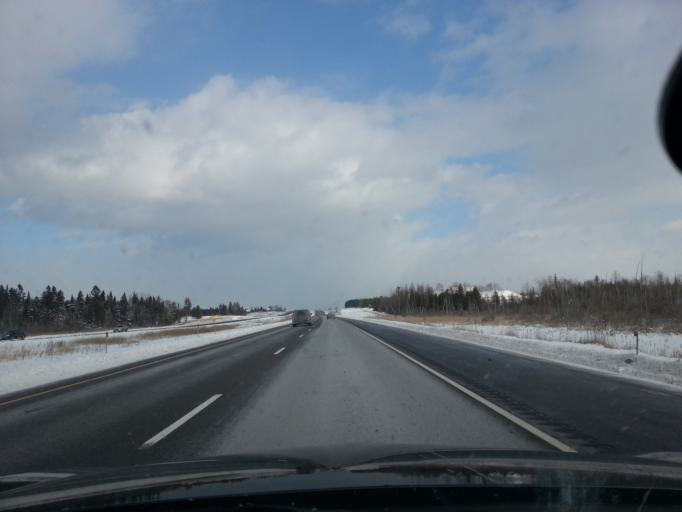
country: CA
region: Ontario
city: Carleton Place
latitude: 45.2271
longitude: -75.9997
